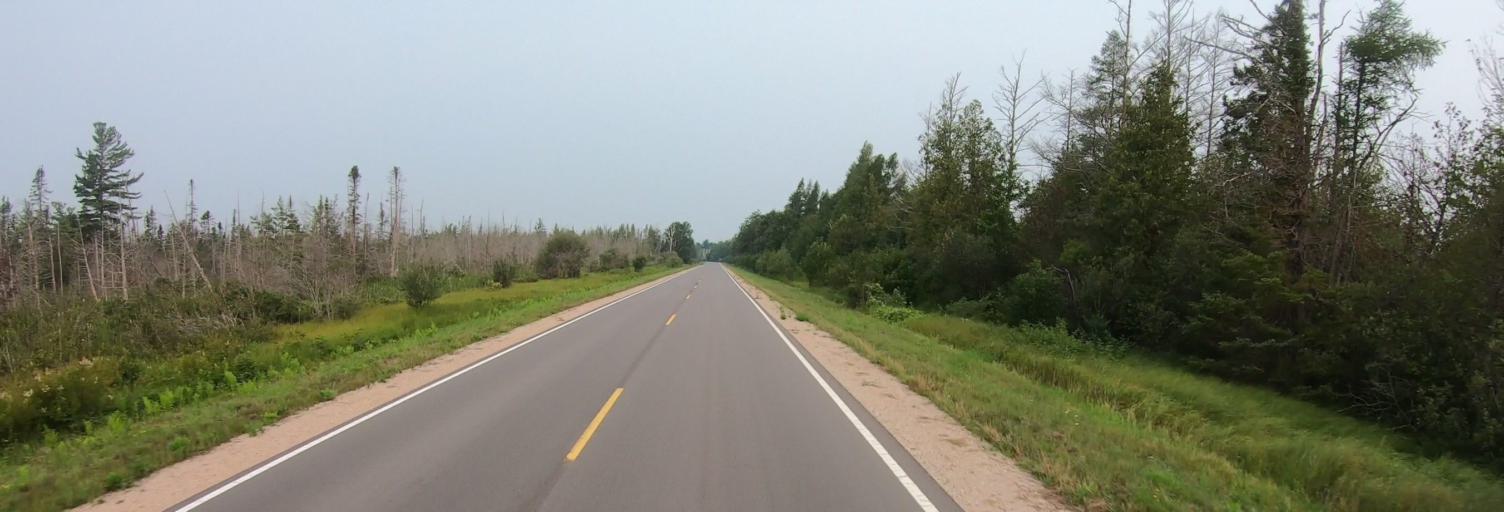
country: US
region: Michigan
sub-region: Luce County
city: Newberry
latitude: 46.4736
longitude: -84.9749
